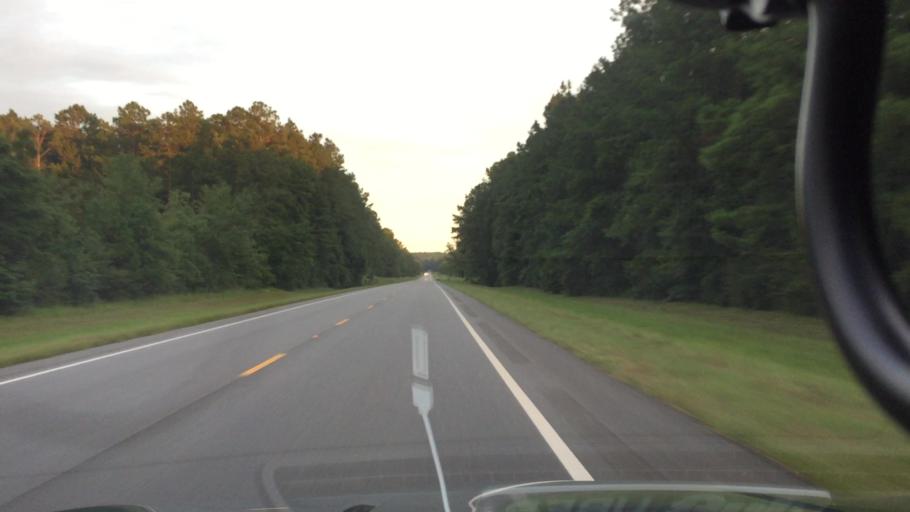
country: US
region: Alabama
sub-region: Coffee County
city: New Brockton
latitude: 31.4853
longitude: -85.9119
